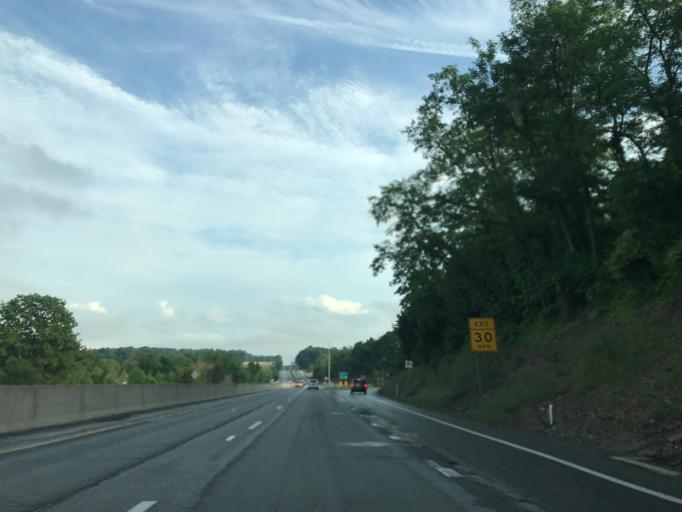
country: US
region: Pennsylvania
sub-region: York County
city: Loganville
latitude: 39.8293
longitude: -76.6851
